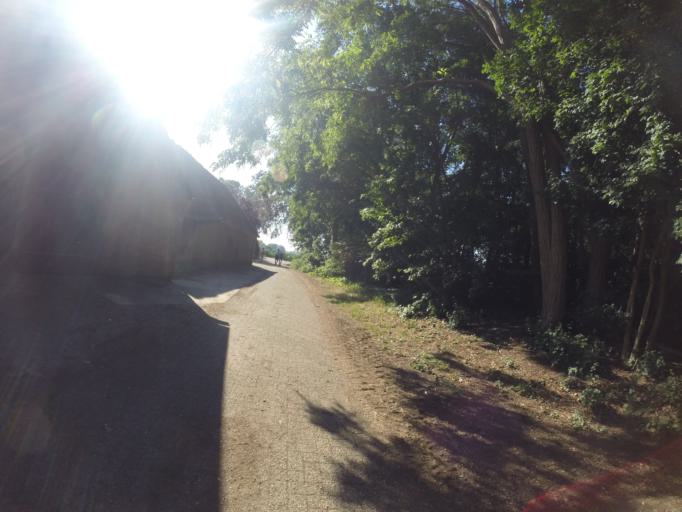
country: NL
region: Gelderland
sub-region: Gemeente Bronckhorst
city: Hengelo
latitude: 52.0817
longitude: 6.3528
